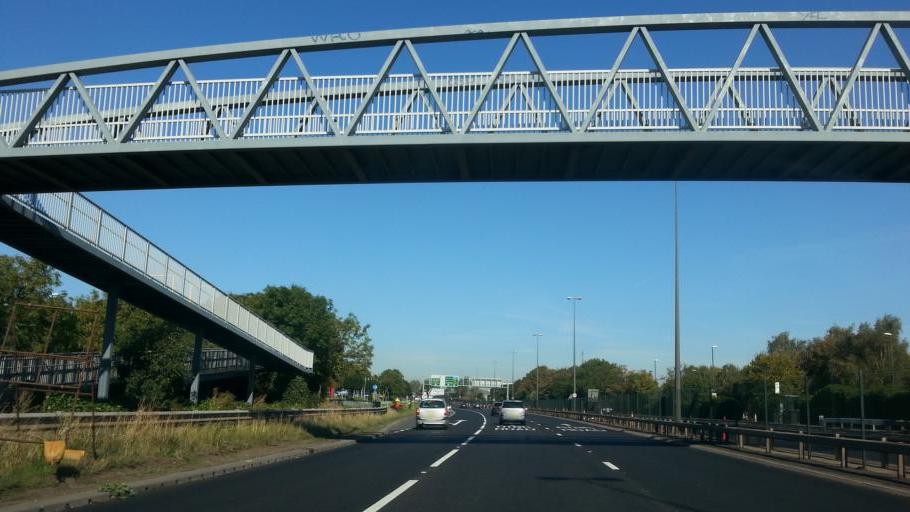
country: GB
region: England
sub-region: Nottingham
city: Nottingham
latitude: 52.9344
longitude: -1.1725
